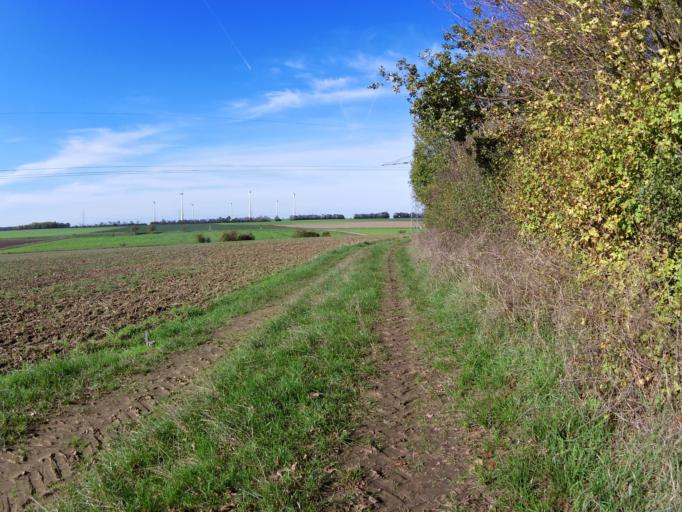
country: DE
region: Bavaria
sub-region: Regierungsbezirk Unterfranken
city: Frickenhausen
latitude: 49.7132
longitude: 10.0845
